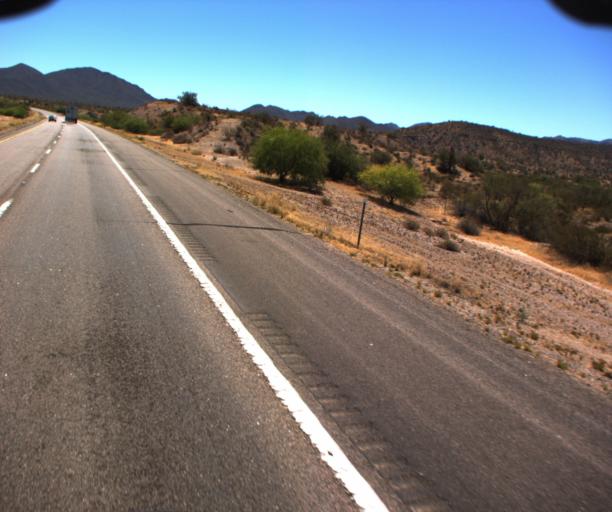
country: US
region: Arizona
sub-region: Maricopa County
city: Fountain Hills
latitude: 33.5808
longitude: -111.6260
